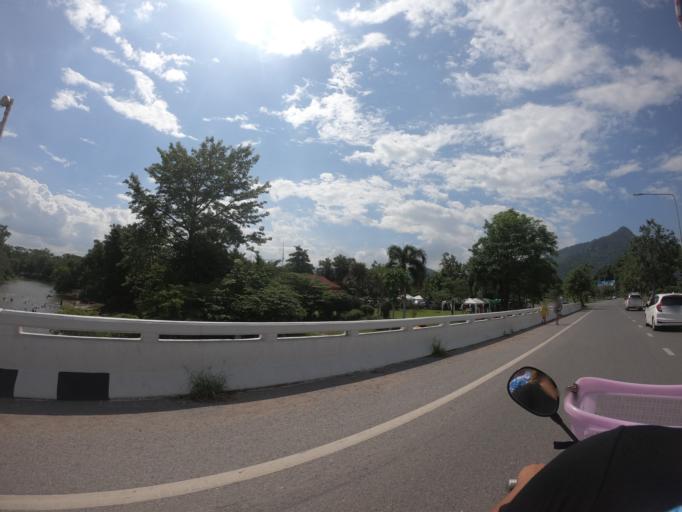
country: TH
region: Nakhon Nayok
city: Nakhon Nayok
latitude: 14.3125
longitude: 101.3152
